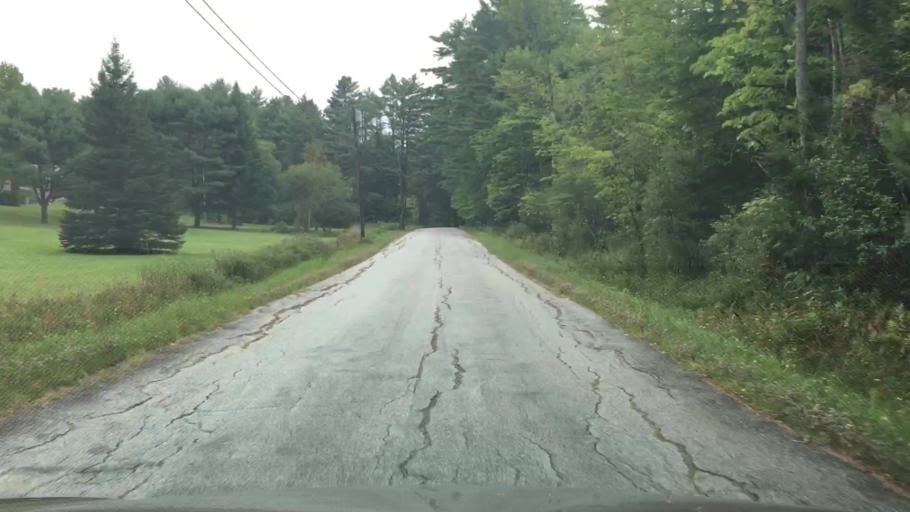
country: US
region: New Hampshire
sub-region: Grafton County
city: Littleton
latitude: 44.3199
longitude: -71.8781
